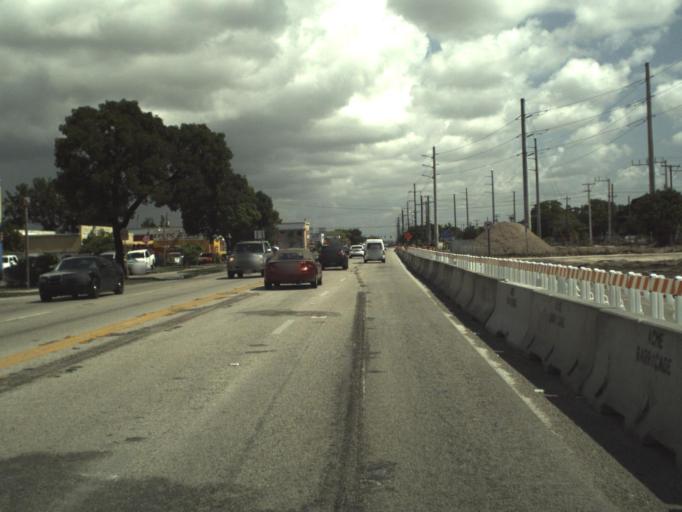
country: US
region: Florida
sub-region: Broward County
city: Pembroke Pines
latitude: 26.0121
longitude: -80.2077
